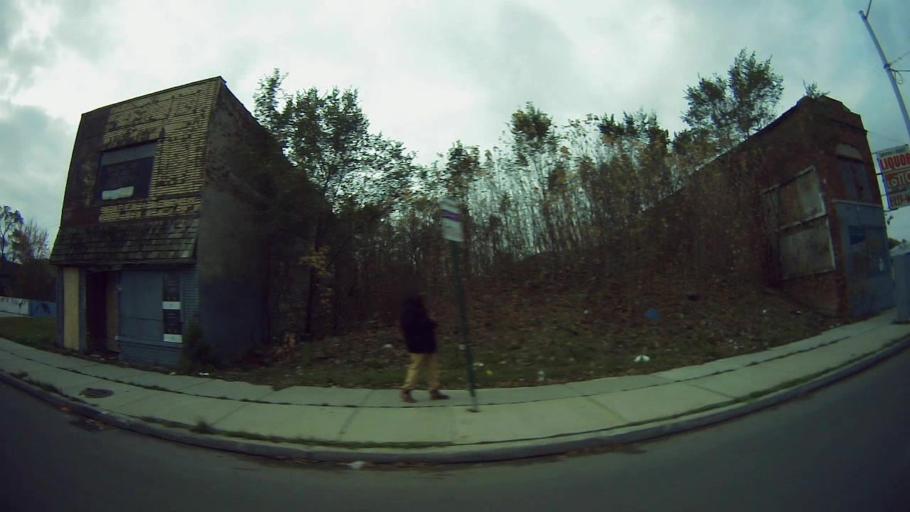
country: US
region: Michigan
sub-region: Wayne County
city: Highland Park
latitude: 42.3809
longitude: -83.1394
